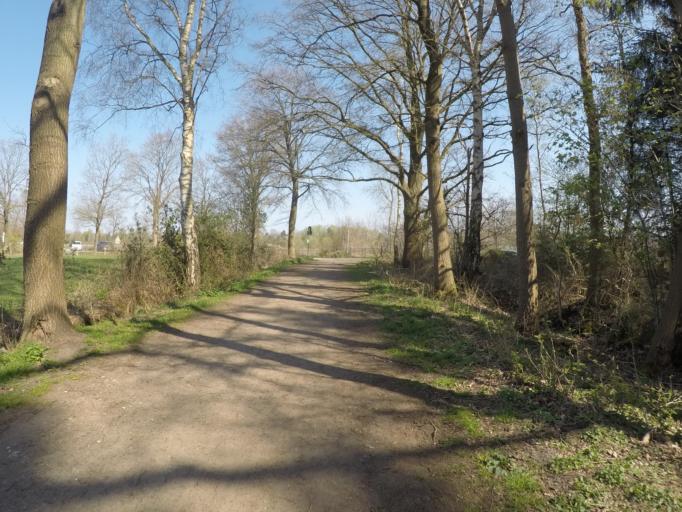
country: DE
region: Schleswig-Holstein
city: Rellingen
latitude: 53.6153
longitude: 9.7850
